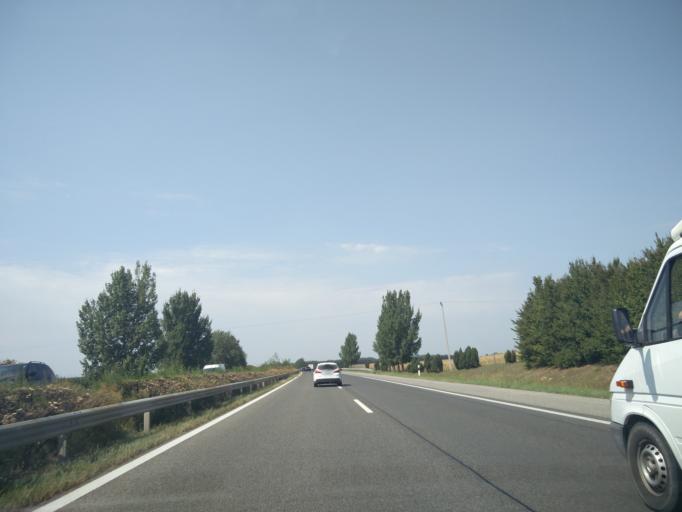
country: HU
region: Bacs-Kiskun
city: Varosfoeld
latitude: 46.8253
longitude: 19.7106
